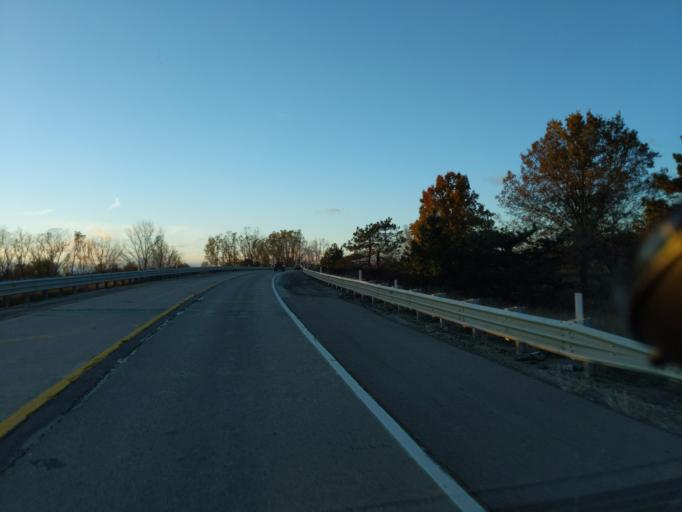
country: US
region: Michigan
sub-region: Eaton County
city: Waverly
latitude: 42.7212
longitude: -84.6650
